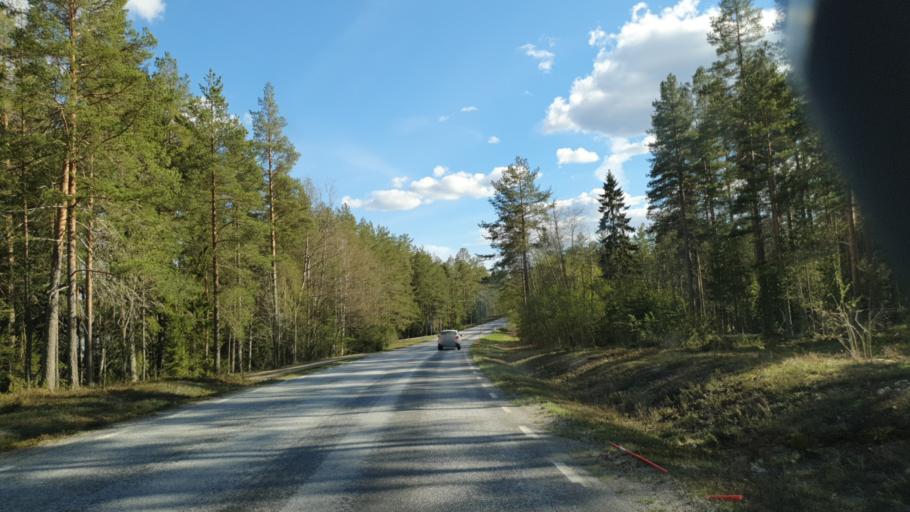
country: SE
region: Vaesterbotten
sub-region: Umea Kommun
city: Roback
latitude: 63.8917
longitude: 20.1574
